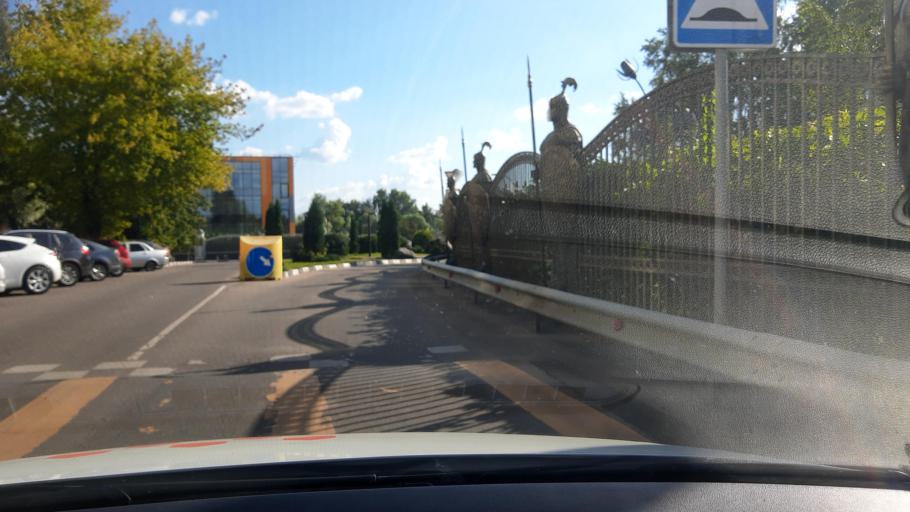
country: RU
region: Moskovskaya
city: Razvilka
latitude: 55.5838
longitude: 37.7374
